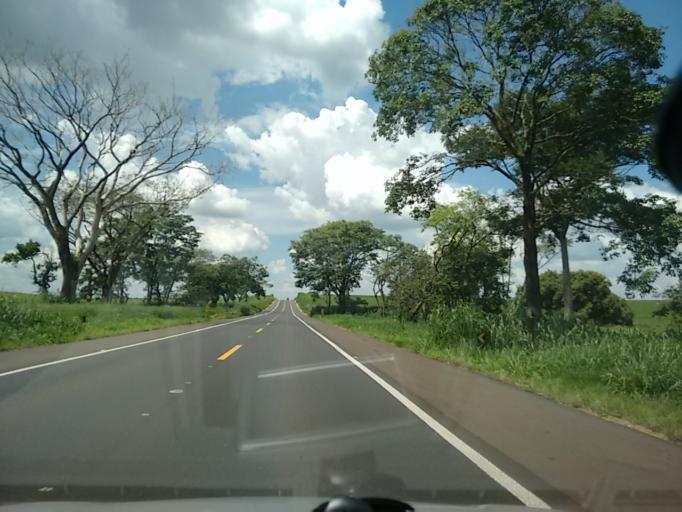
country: BR
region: Sao Paulo
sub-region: Osvaldo Cruz
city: Osvaldo Cruz
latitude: -21.8751
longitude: -50.8590
